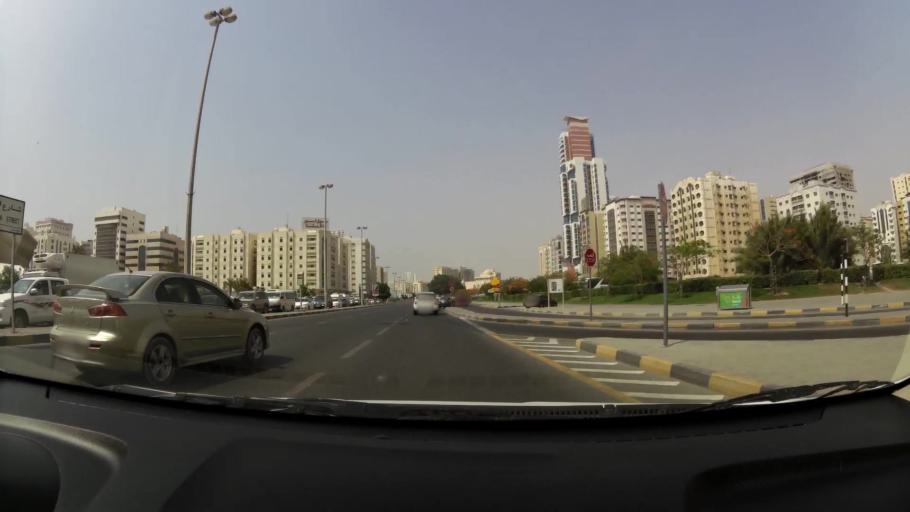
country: AE
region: Ash Shariqah
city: Sharjah
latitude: 25.3481
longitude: 55.3885
